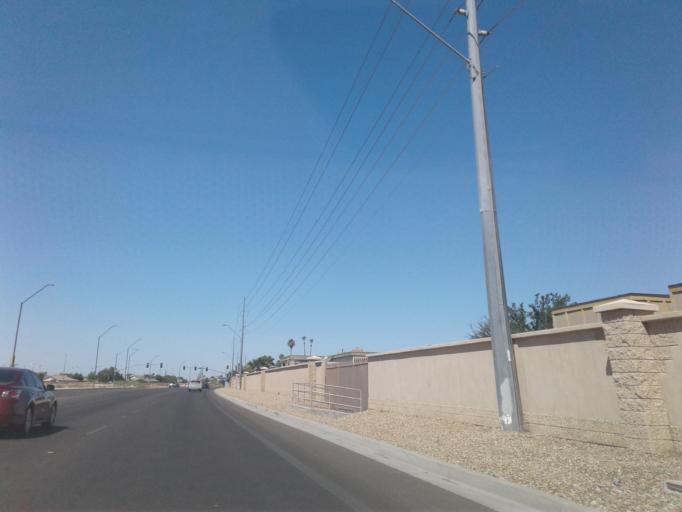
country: US
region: Arizona
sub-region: Maricopa County
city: Litchfield Park
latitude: 33.4881
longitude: -112.3526
